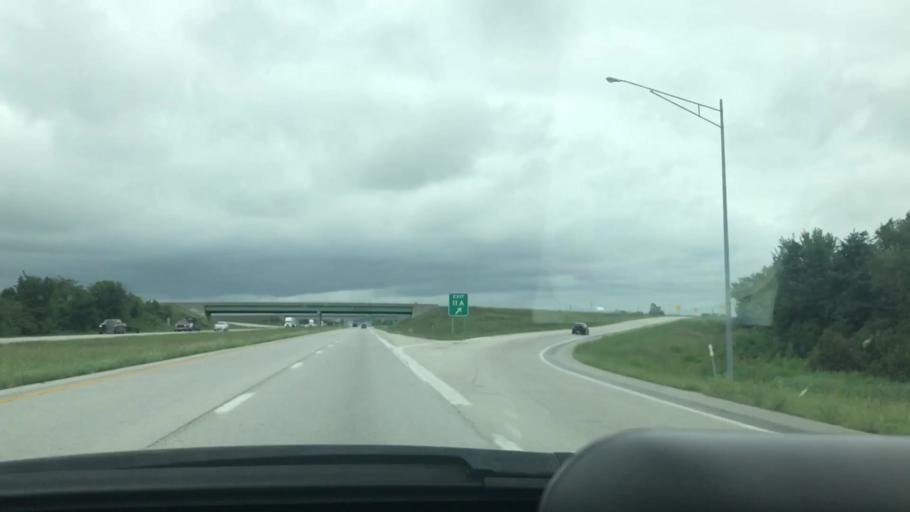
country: US
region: Missouri
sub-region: Jasper County
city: Duenweg
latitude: 37.0592
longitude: -94.4332
